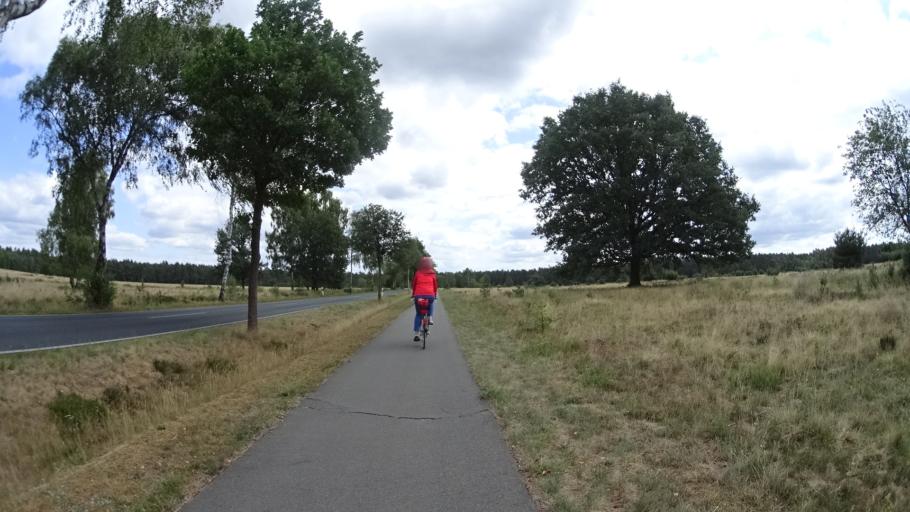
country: DE
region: Lower Saxony
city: Handeloh
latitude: 53.2379
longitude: 9.8752
